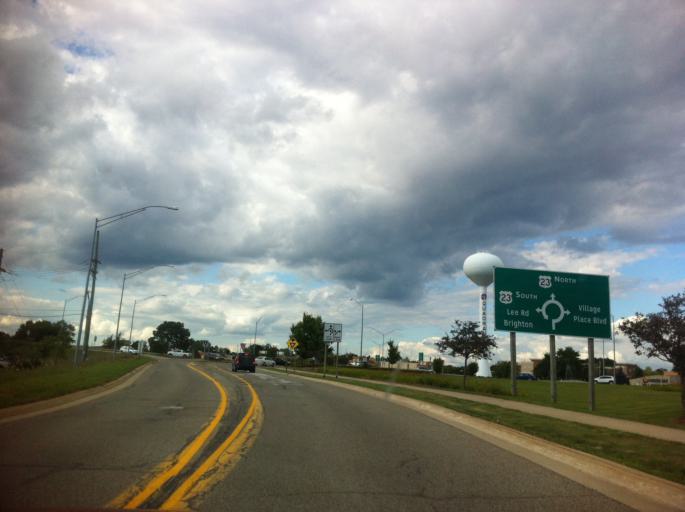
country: US
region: Michigan
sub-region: Livingston County
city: Brighton
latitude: 42.5035
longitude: -83.7567
